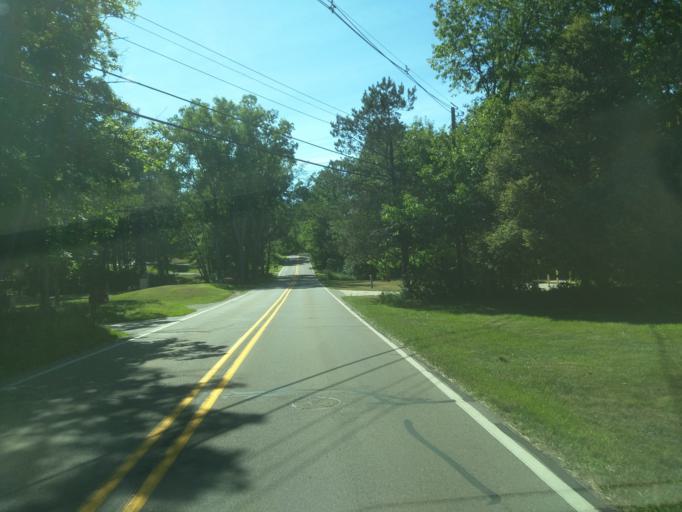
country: US
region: Michigan
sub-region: Eaton County
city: Waverly
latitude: 42.7645
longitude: -84.6171
